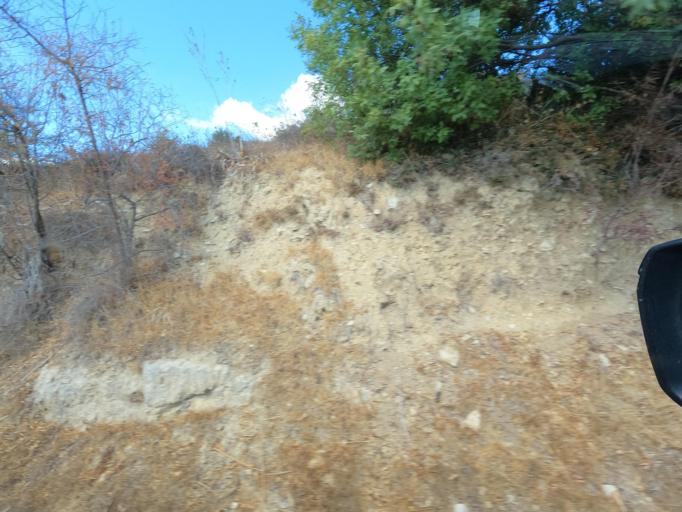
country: CY
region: Pafos
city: Mesogi
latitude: 34.8418
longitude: 32.5354
